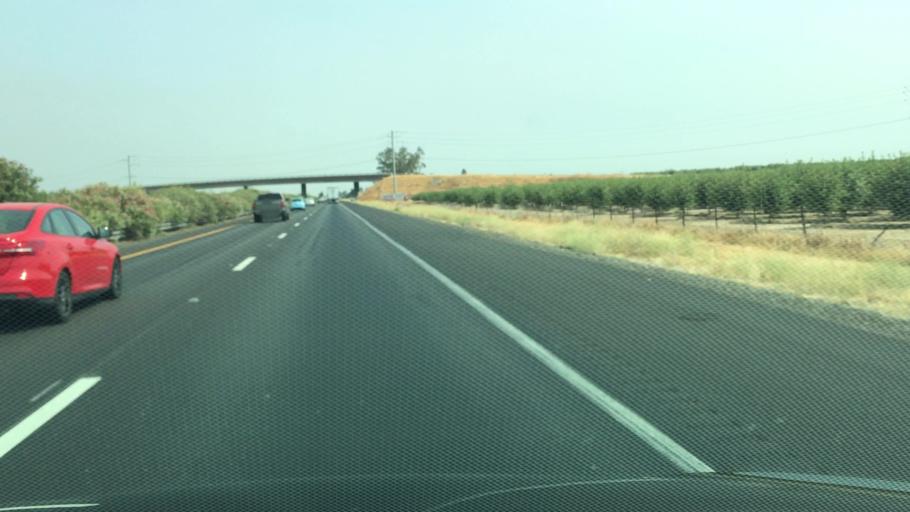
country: US
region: California
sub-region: Madera County
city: Parksdale
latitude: 36.9116
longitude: -120.0085
